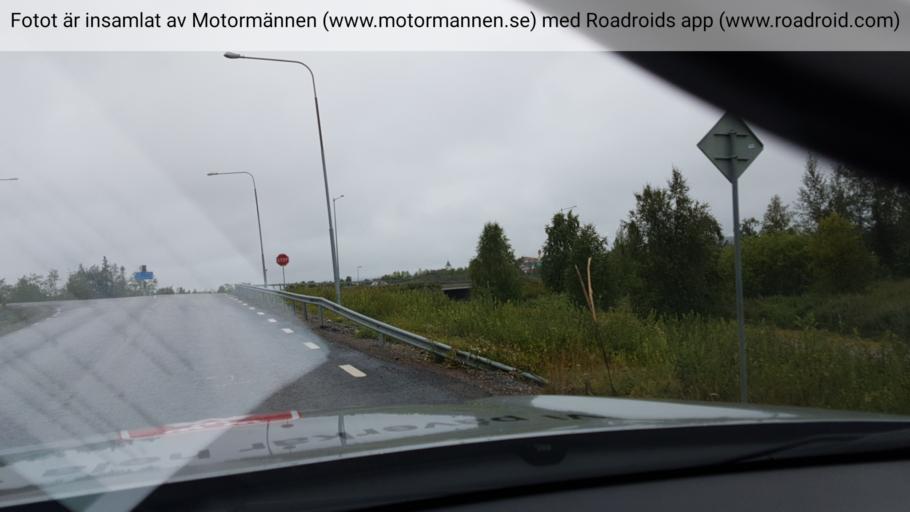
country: SE
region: Norrbotten
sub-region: Gallivare Kommun
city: Gaellivare
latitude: 67.1267
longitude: 20.6714
